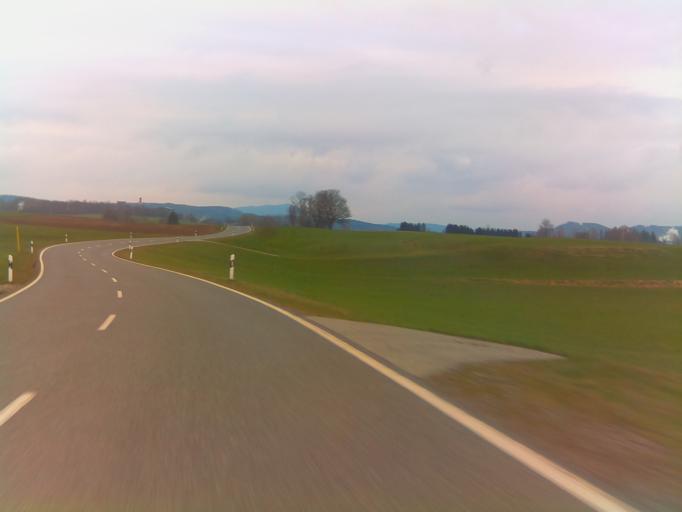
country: DE
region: Bavaria
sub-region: Upper Bavaria
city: Schwabsoien
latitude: 47.8346
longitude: 10.8414
